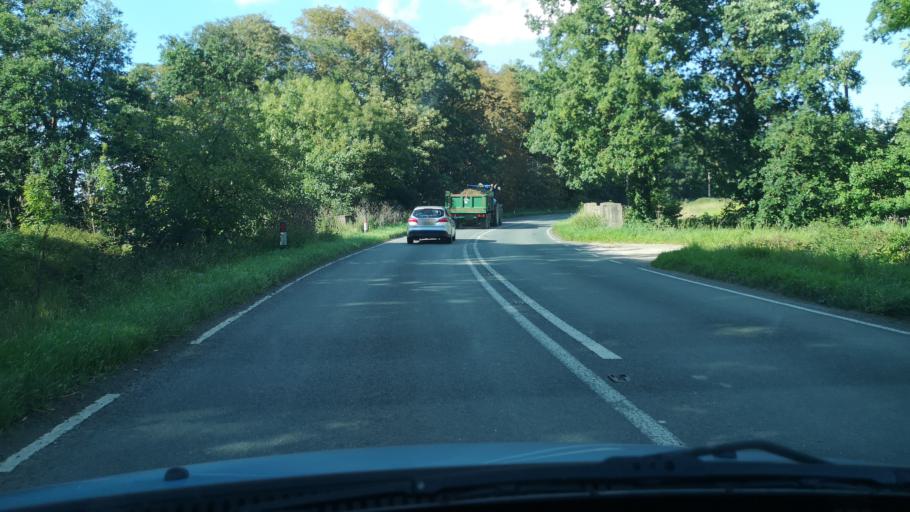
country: GB
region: England
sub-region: North Lincolnshire
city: Belton
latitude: 53.5790
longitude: -0.8211
